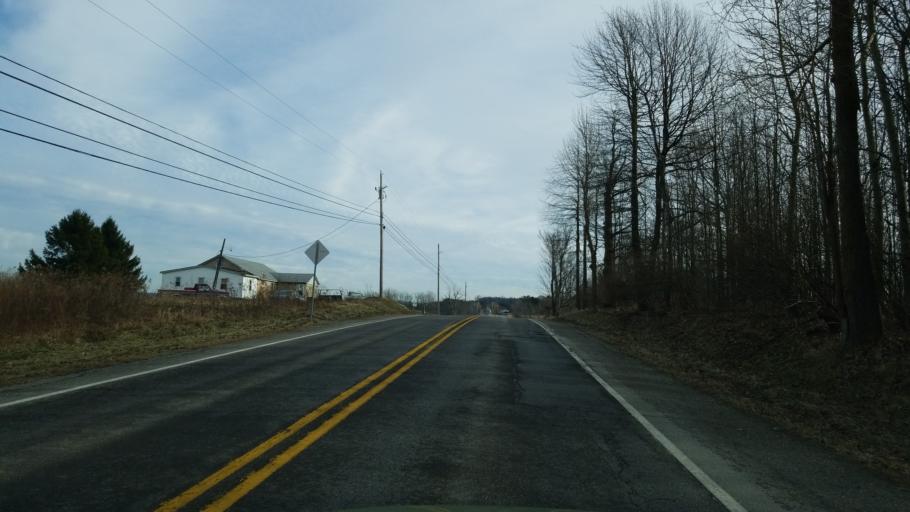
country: US
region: Pennsylvania
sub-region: Indiana County
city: Johnsonburg
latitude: 40.9157
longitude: -78.8401
